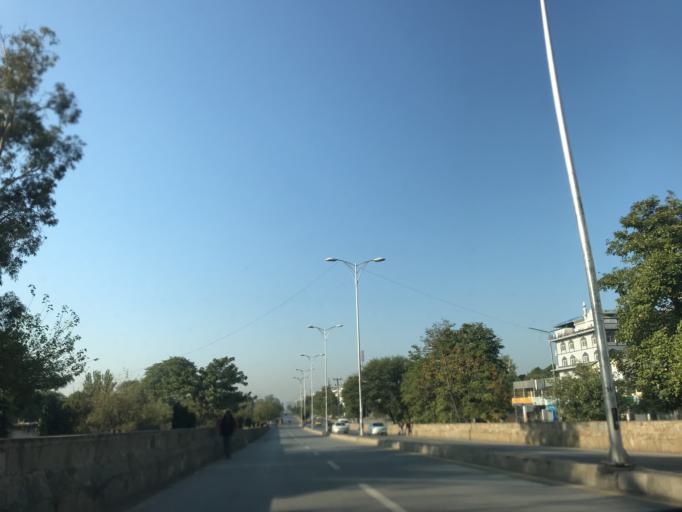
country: PK
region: Islamabad
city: Islamabad
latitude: 33.7222
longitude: 73.0825
